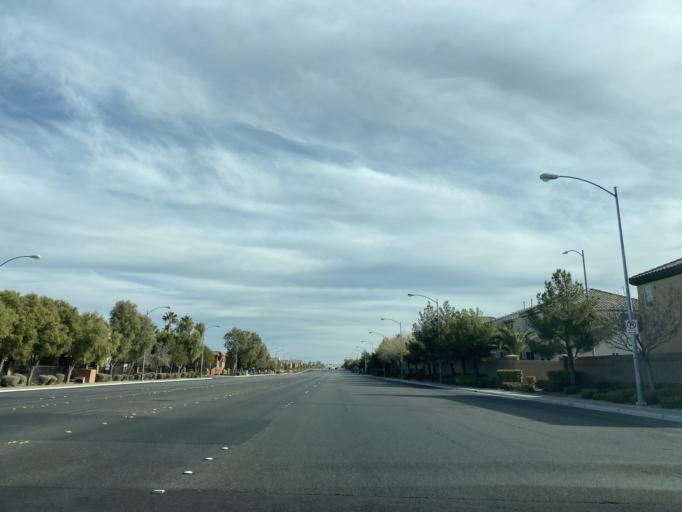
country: US
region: Nevada
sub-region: Clark County
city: Summerlin South
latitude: 36.0701
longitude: -115.3062
